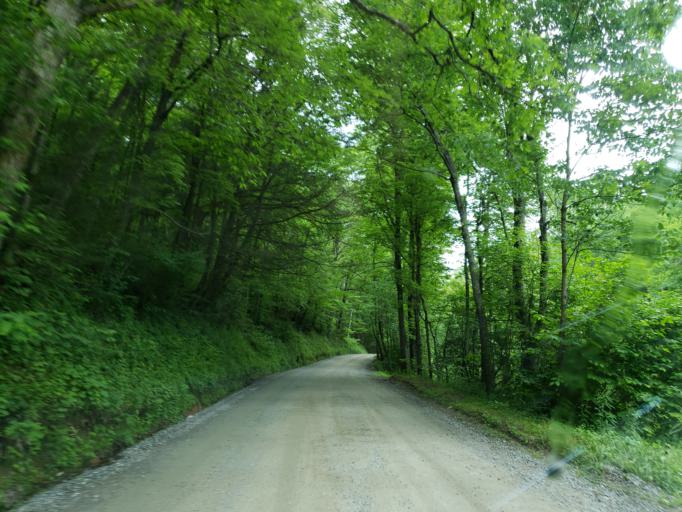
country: US
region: Georgia
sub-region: Fannin County
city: Blue Ridge
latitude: 34.8433
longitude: -84.4160
